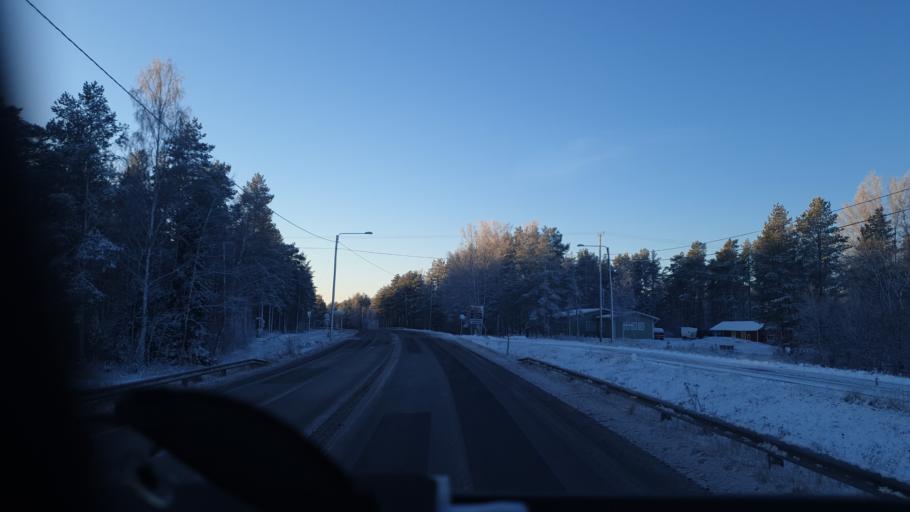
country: FI
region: Northern Ostrobothnia
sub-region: Ylivieska
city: Kalajoki
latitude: 64.2098
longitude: 23.7722
